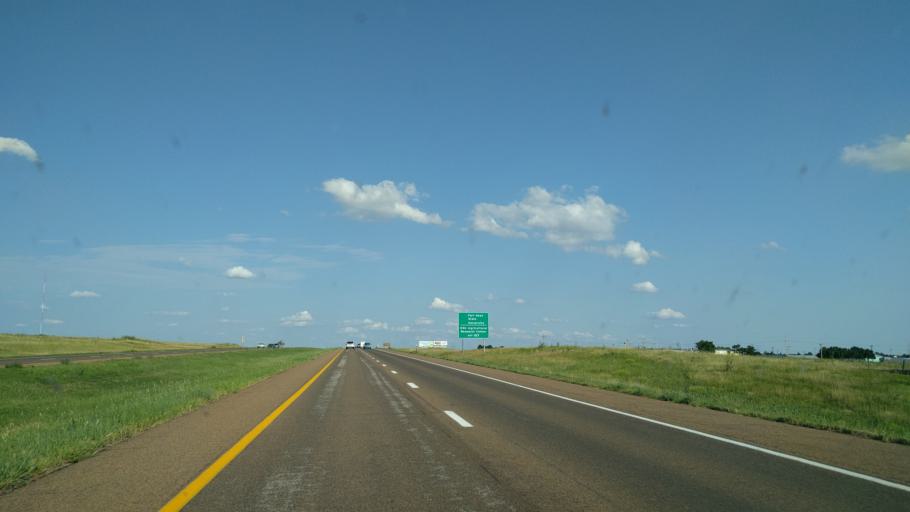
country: US
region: Kansas
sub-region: Ellis County
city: Hays
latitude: 38.9169
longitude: -99.3677
